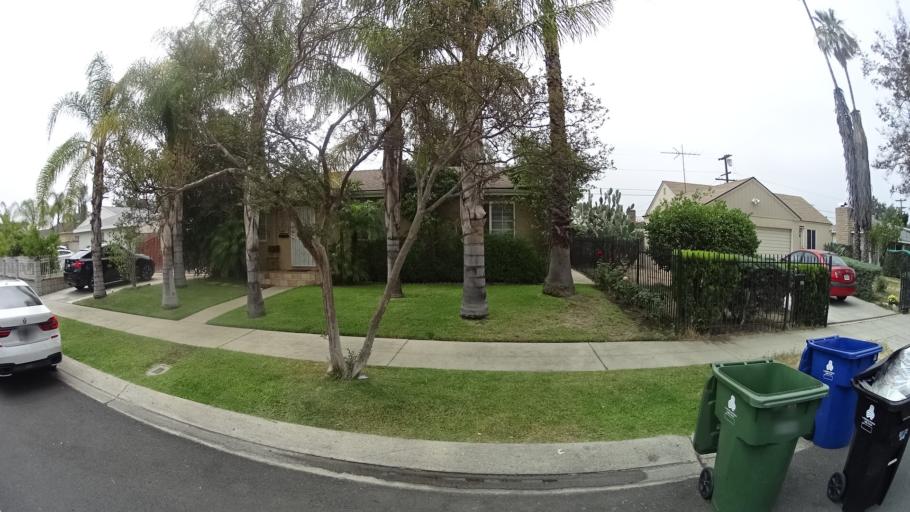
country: US
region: California
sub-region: Los Angeles County
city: North Hollywood
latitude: 34.1910
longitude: -118.4110
